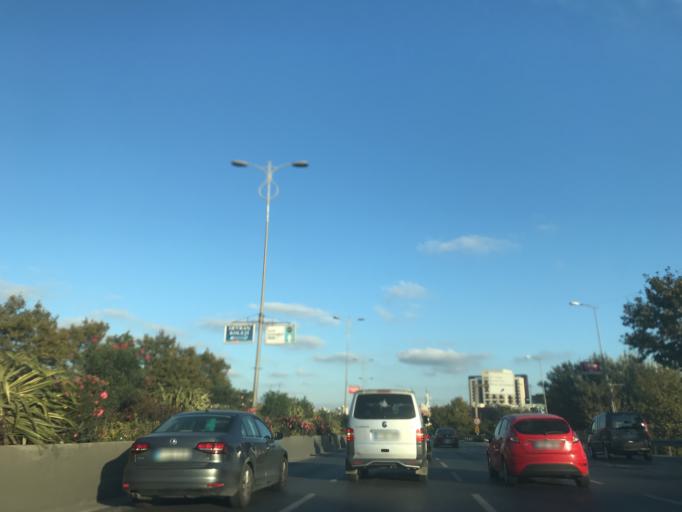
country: TR
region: Istanbul
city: Esenler
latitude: 41.0462
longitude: 28.8812
